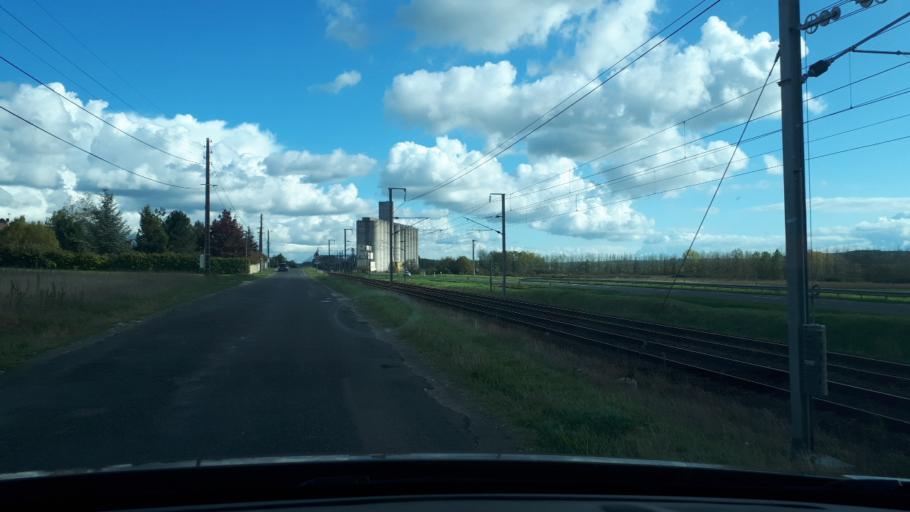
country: FR
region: Centre
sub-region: Departement du Loir-et-Cher
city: Mareuil-sur-Cher
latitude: 47.2991
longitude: 1.3572
